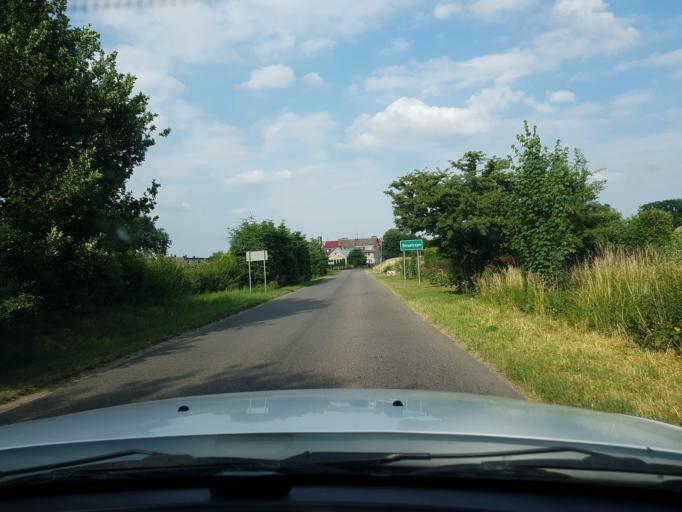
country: PL
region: West Pomeranian Voivodeship
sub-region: Powiat gryfinski
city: Chojna
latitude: 53.0049
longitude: 14.5126
